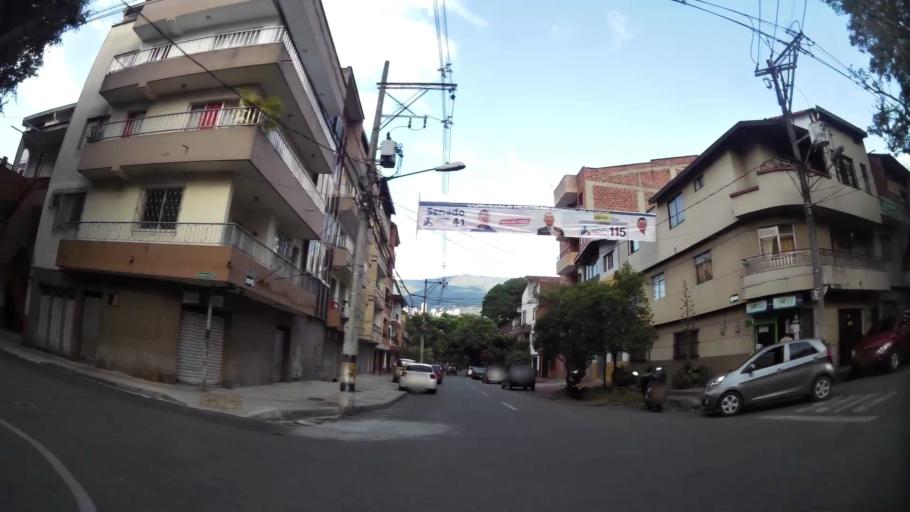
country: CO
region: Antioquia
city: Envigado
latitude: 6.1745
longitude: -75.5839
